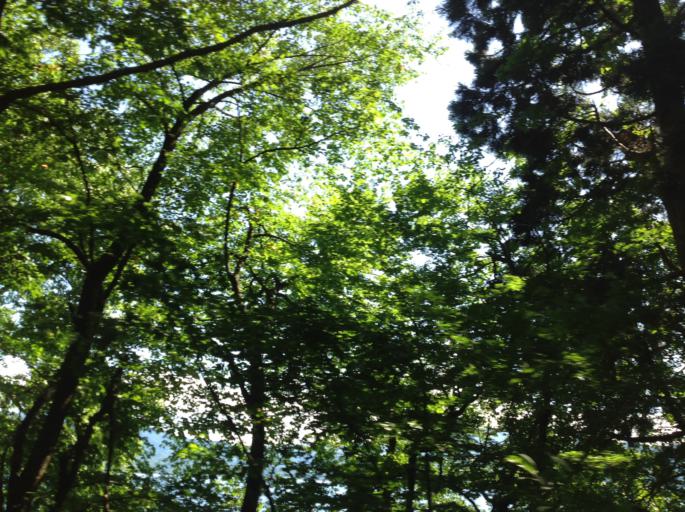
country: JP
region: Akita
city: Kakunodatemachi
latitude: 39.7029
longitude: 140.6442
